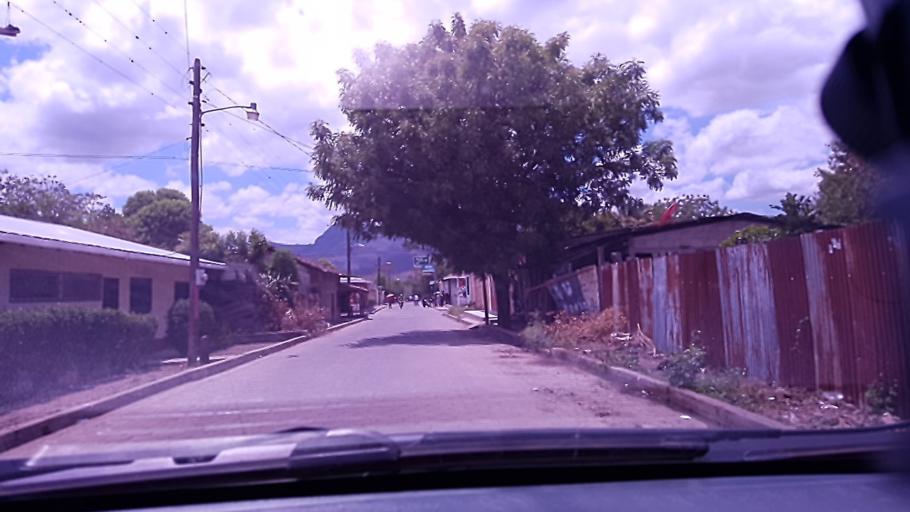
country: NI
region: Esteli
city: Condega
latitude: 13.3632
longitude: -86.3969
